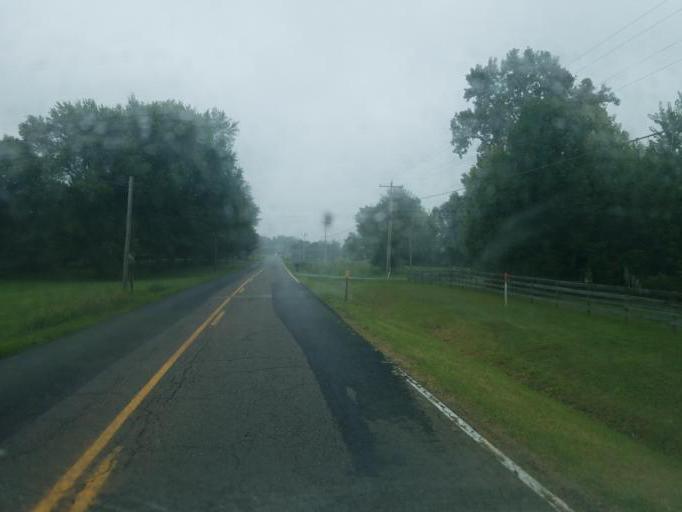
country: US
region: Ohio
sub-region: Licking County
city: Johnstown
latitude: 40.1756
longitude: -82.6917
